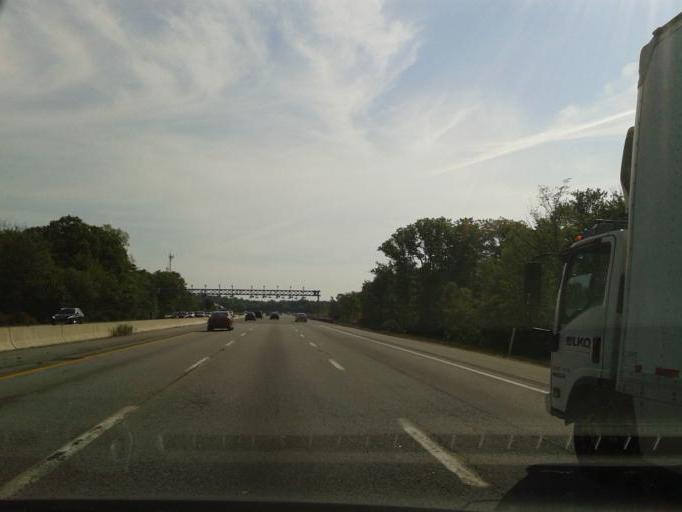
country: US
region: Massachusetts
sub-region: Middlesex County
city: Cochituate
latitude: 42.3304
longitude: -71.3250
